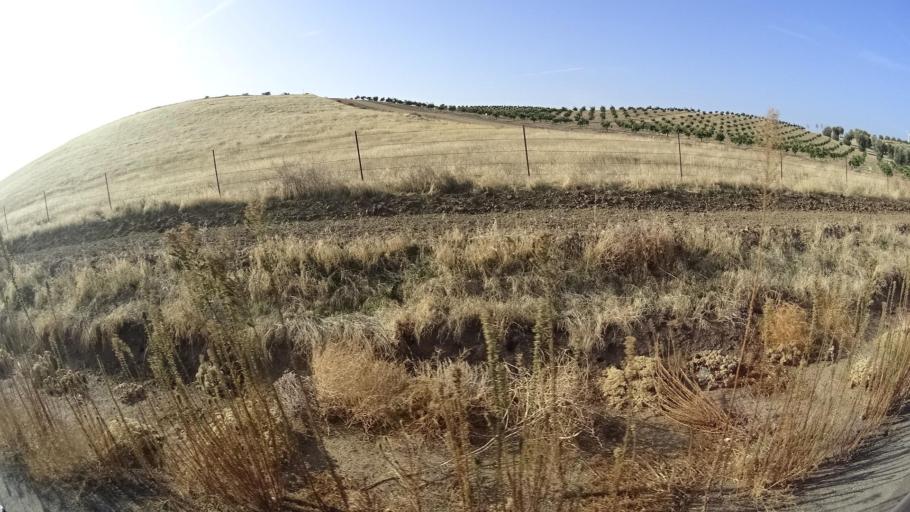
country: US
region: California
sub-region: Tulare County
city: Richgrove
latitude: 35.6431
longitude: -119.0497
